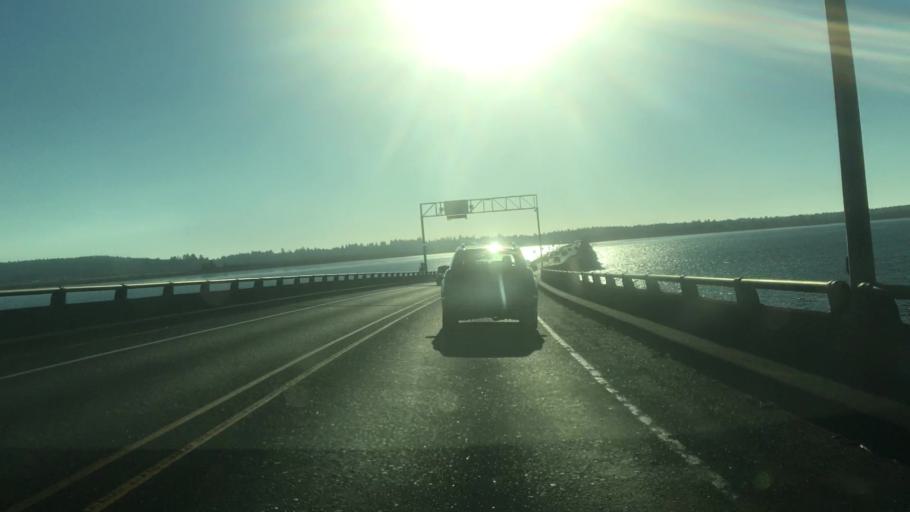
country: US
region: Oregon
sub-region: Clatsop County
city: Astoria
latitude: 46.1739
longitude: -123.8715
